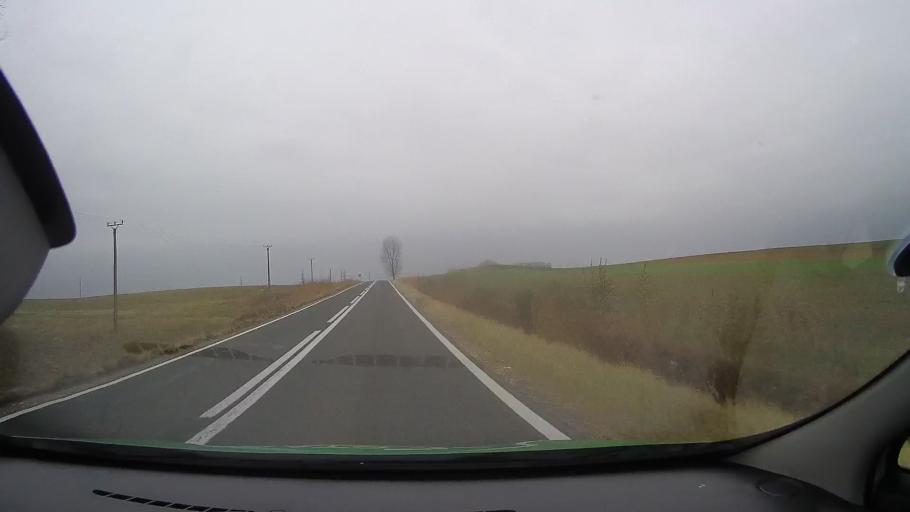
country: RO
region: Constanta
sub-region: Comuna Ciobanu
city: Ciobanu
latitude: 44.6986
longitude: 28.0016
